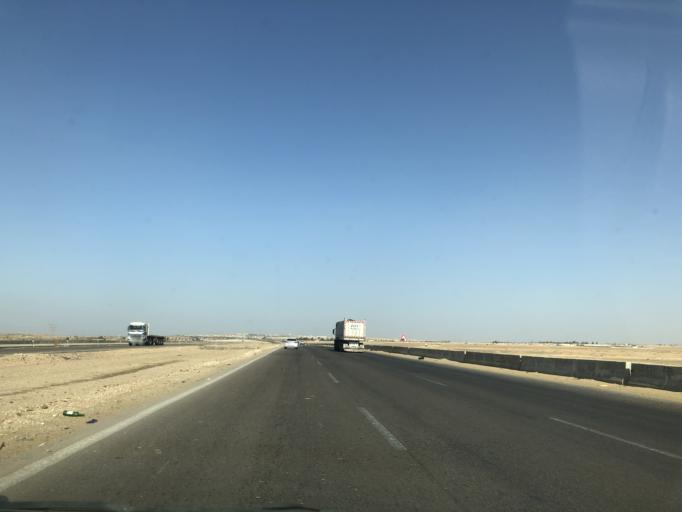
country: EG
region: Muhafazat al Minufiyah
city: Ashmun
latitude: 30.0678
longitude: 30.8900
